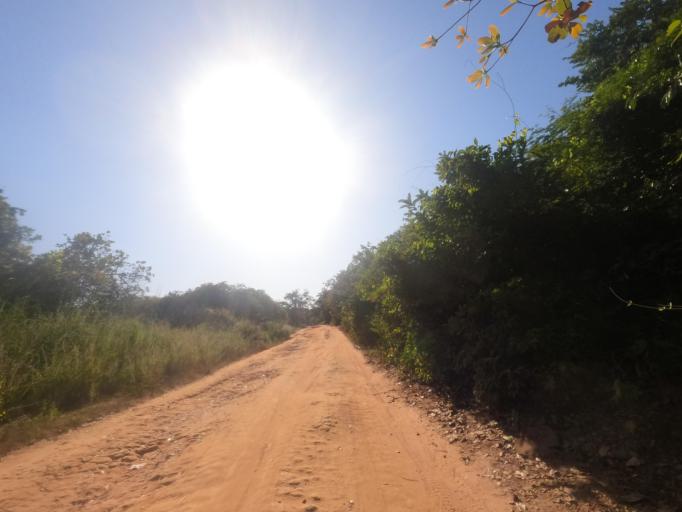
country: GW
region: Cacheu
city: Cacheu
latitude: 12.4010
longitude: -16.2066
